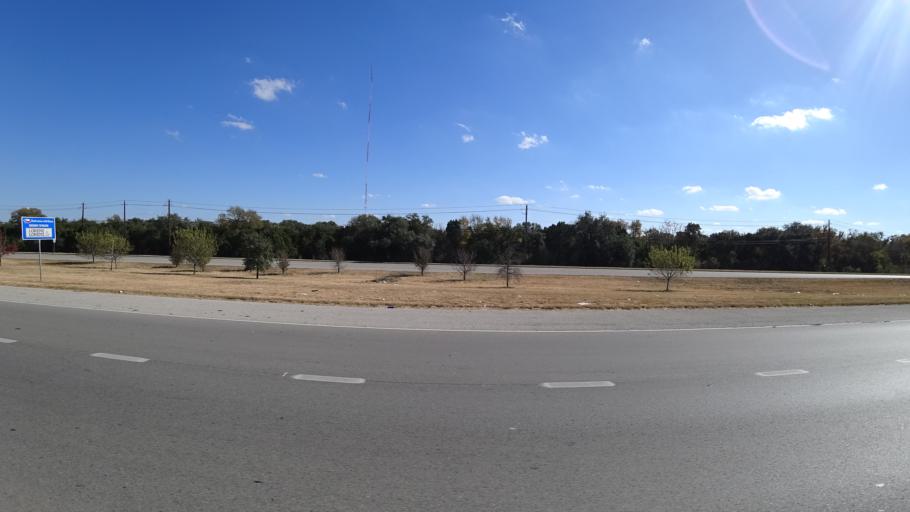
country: US
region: Texas
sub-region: Travis County
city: Rollingwood
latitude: 30.2253
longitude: -97.8320
